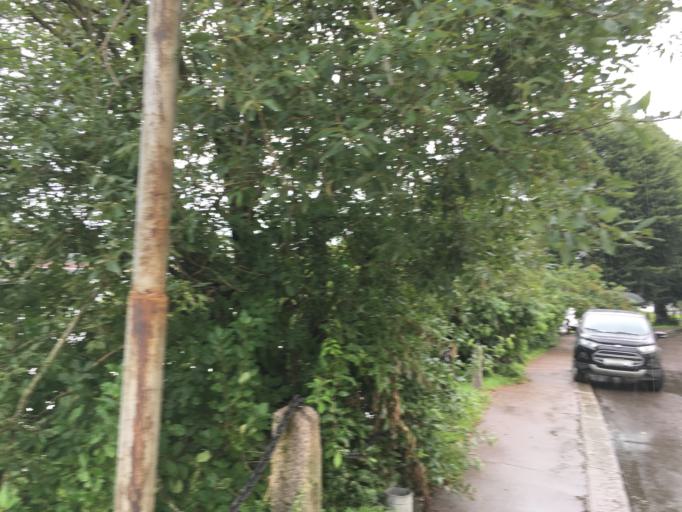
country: RU
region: Leningrad
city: Vyborg
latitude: 60.7148
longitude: 28.7311
